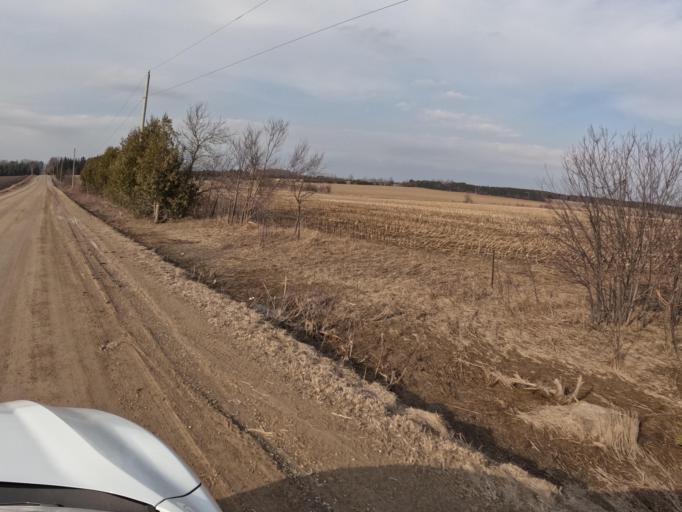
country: CA
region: Ontario
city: Orangeville
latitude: 43.9059
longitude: -80.2691
